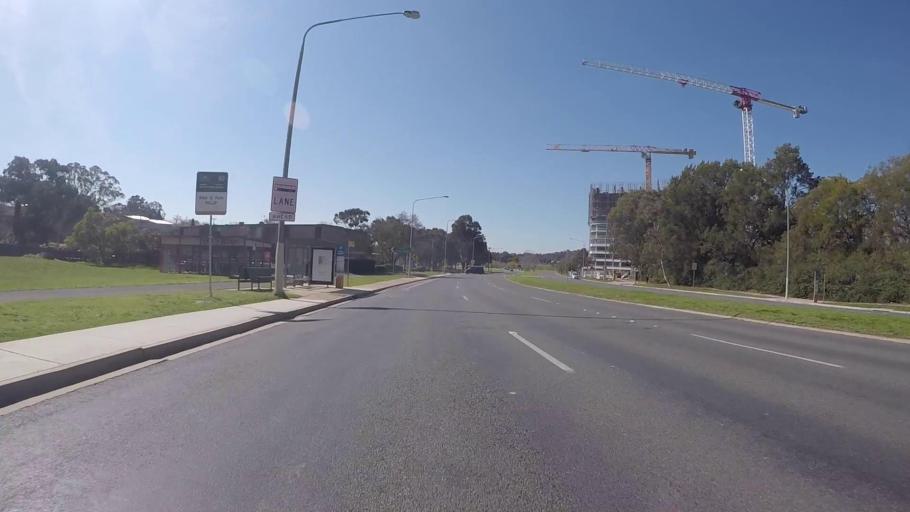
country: AU
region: Australian Capital Territory
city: Forrest
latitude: -35.3393
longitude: 149.0827
